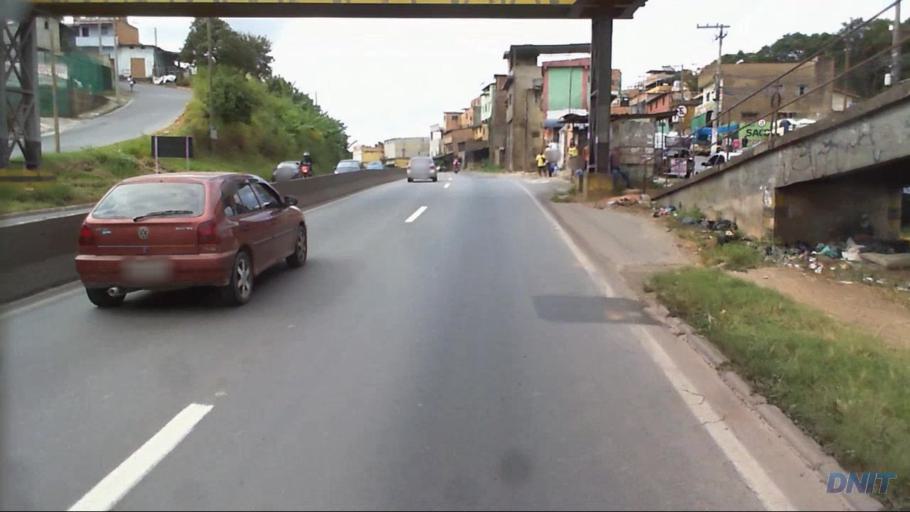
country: BR
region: Minas Gerais
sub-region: Belo Horizonte
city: Belo Horizonte
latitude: -19.8531
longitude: -43.8894
